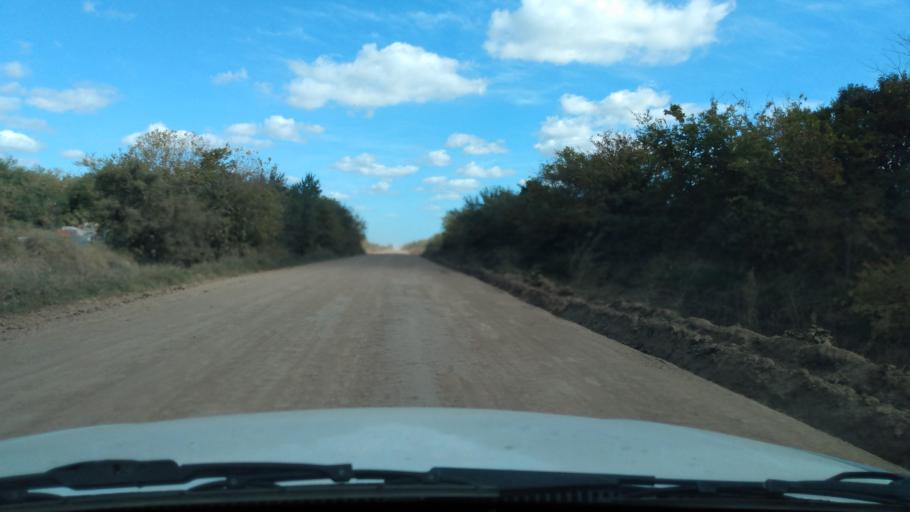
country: AR
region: Buenos Aires
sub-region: Partido de Navarro
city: Navarro
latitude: -35.0309
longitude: -59.4508
